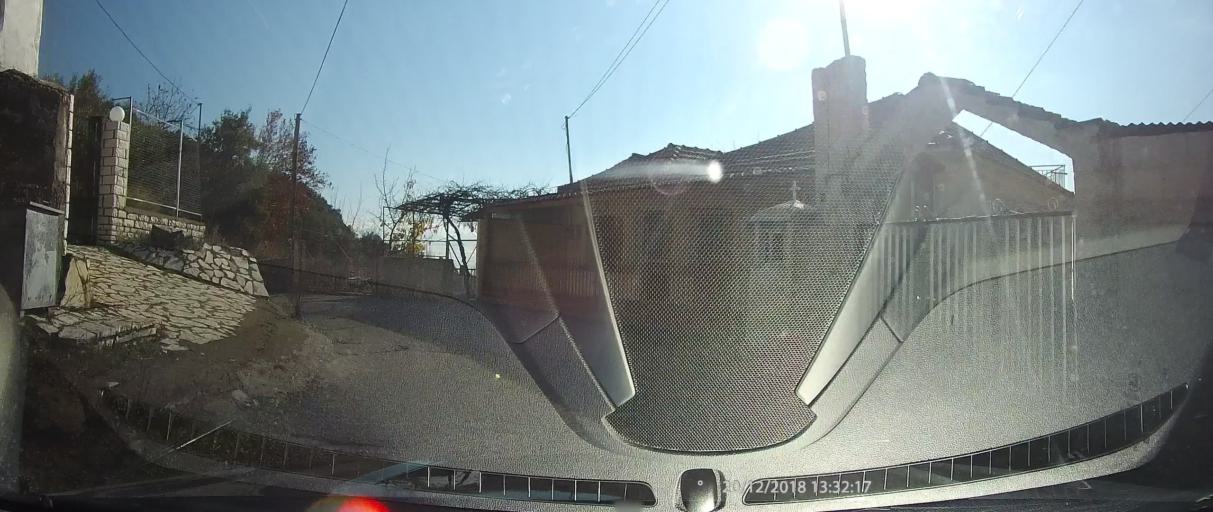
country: GR
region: West Greece
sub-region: Nomos Aitolias kai Akarnanias
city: Paravola
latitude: 38.6295
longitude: 21.5874
